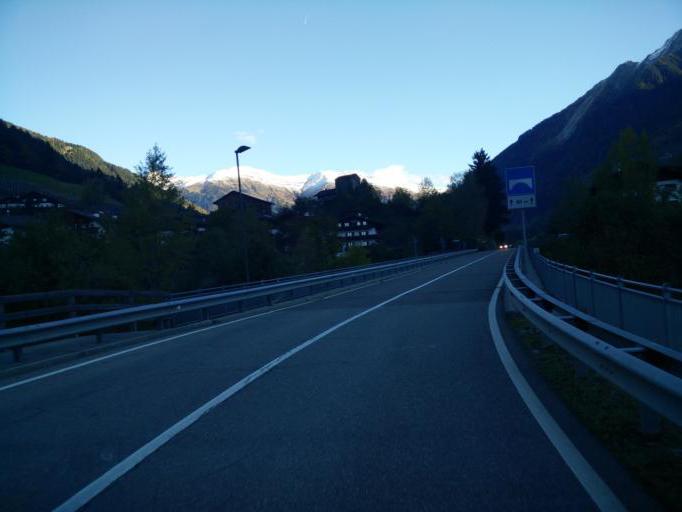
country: IT
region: Trentino-Alto Adige
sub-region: Bolzano
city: San Martino in Passiria
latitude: 46.7678
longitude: 11.2151
